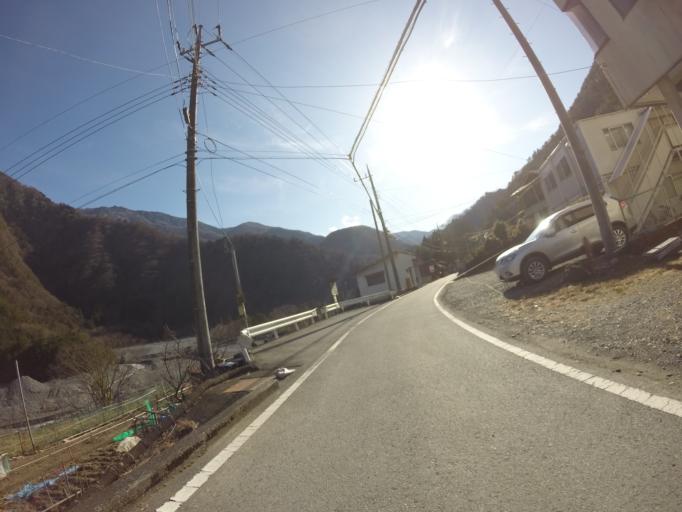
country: JP
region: Yamanashi
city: Ryuo
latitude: 35.3971
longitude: 138.3236
